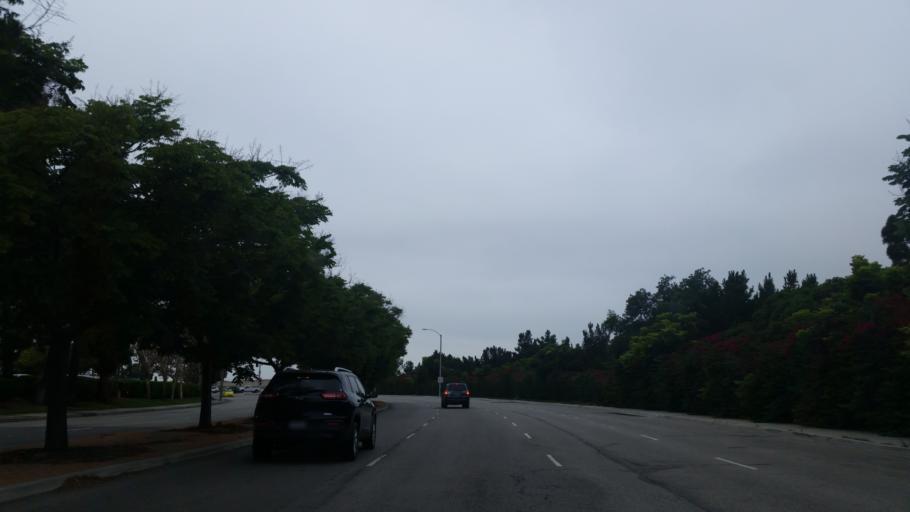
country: US
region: California
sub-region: Los Angeles County
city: Signal Hill
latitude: 33.8119
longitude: -118.1372
